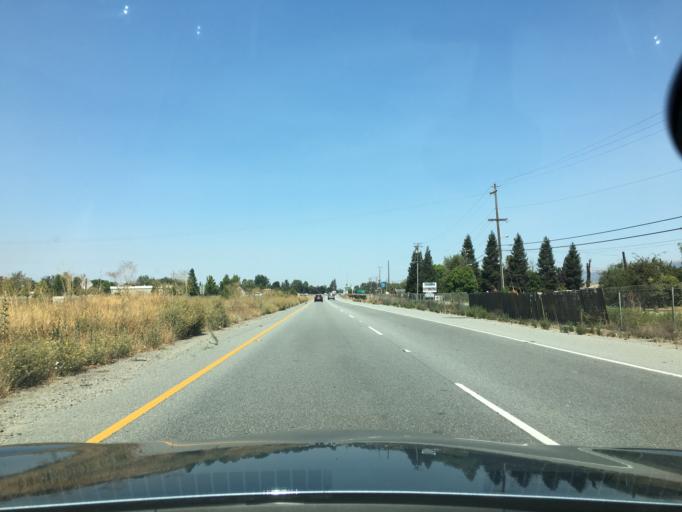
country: US
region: California
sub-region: Santa Clara County
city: Gilroy
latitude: 36.9774
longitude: -121.5560
